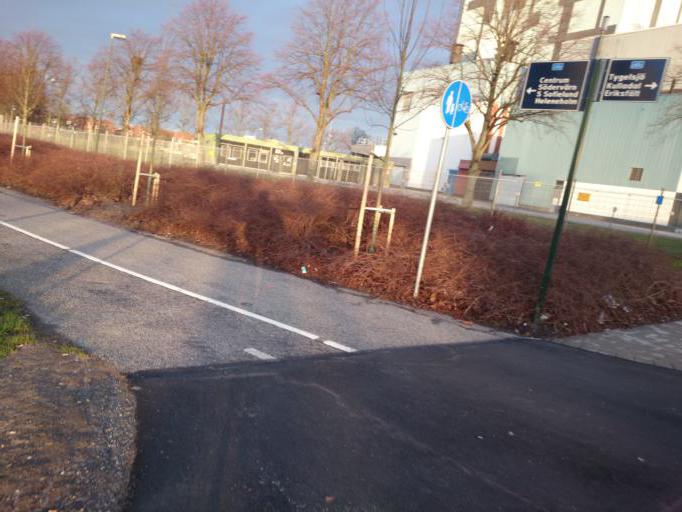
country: SE
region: Skane
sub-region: Malmo
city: Malmoe
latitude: 55.5780
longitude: 13.0101
